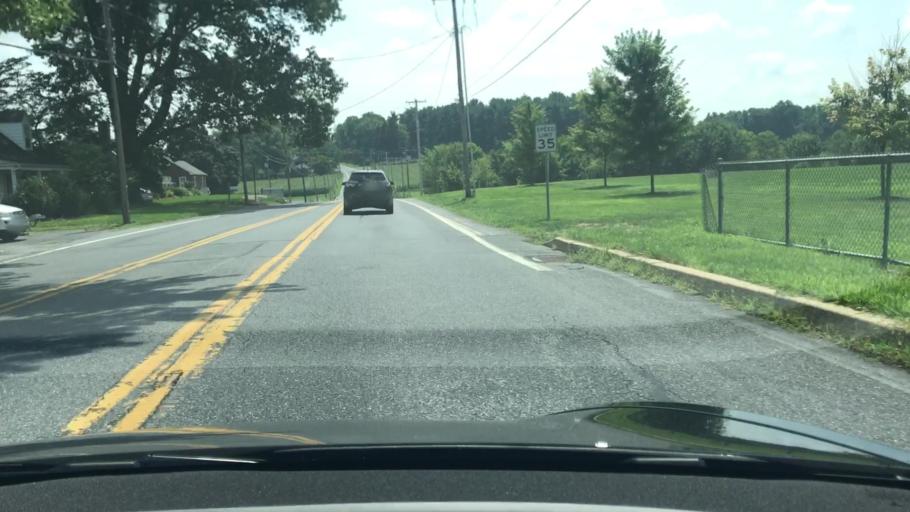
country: US
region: Pennsylvania
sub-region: Lancaster County
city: Landisville
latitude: 40.0854
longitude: -76.4091
